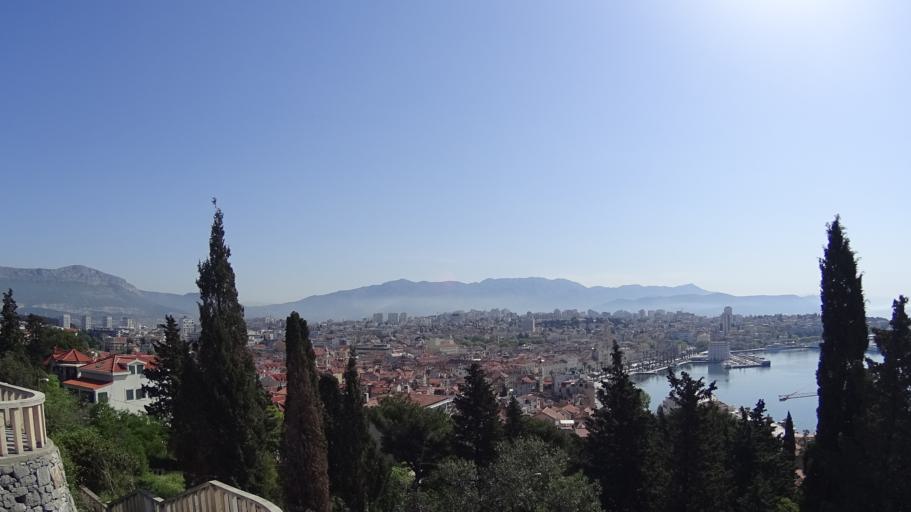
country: HR
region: Splitsko-Dalmatinska
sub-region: Grad Split
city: Split
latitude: 43.5077
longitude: 16.4303
